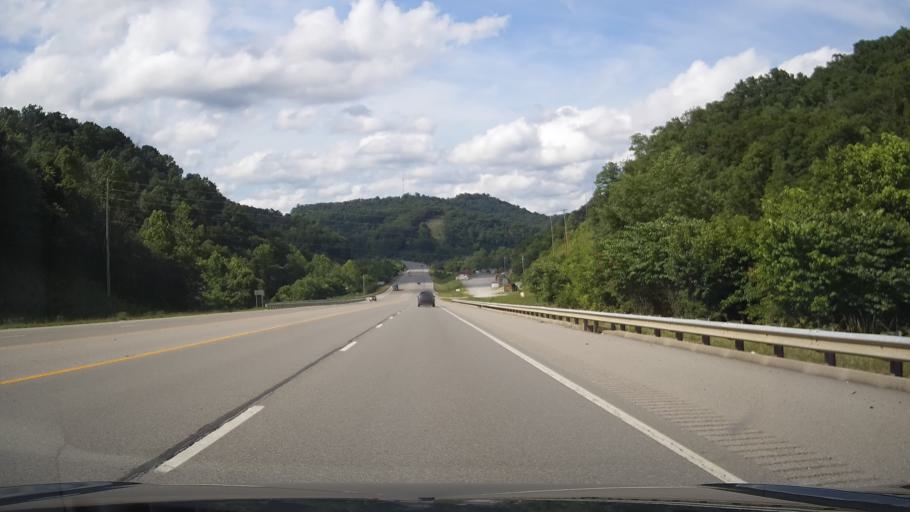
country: US
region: Kentucky
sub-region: Floyd County
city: Prestonsburg
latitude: 37.6744
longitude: -82.7931
